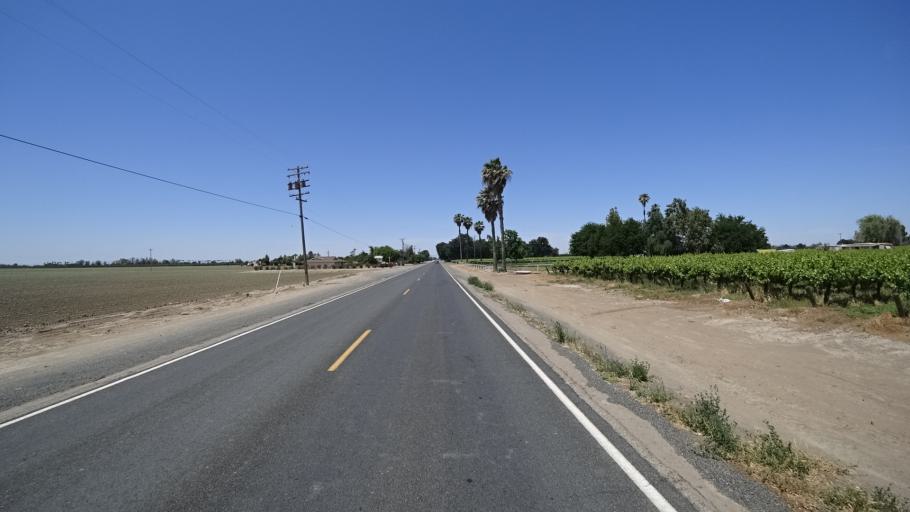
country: US
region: California
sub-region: Kings County
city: Lemoore
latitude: 36.3426
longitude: -119.7926
